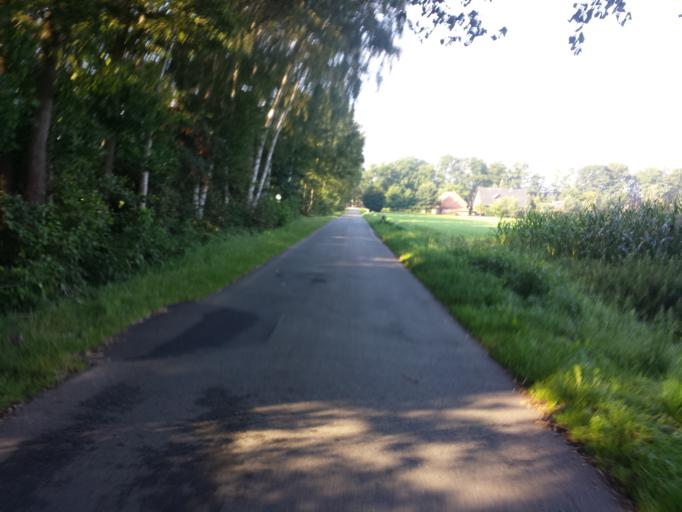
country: DE
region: North Rhine-Westphalia
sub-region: Regierungsbezirk Detmold
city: Guetersloh
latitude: 51.9334
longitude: 8.3147
